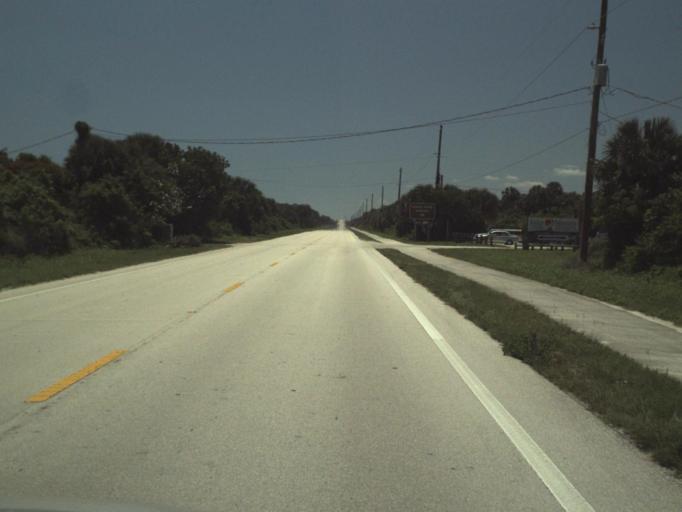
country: US
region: Florida
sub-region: Brevard County
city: Micco
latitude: 27.8766
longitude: -80.4569
